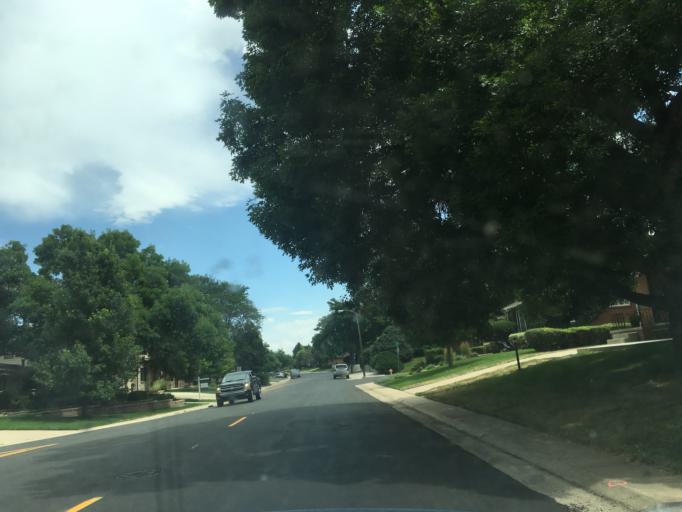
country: US
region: Colorado
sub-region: Arapahoe County
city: Sheridan
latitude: 39.6767
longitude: -105.0487
